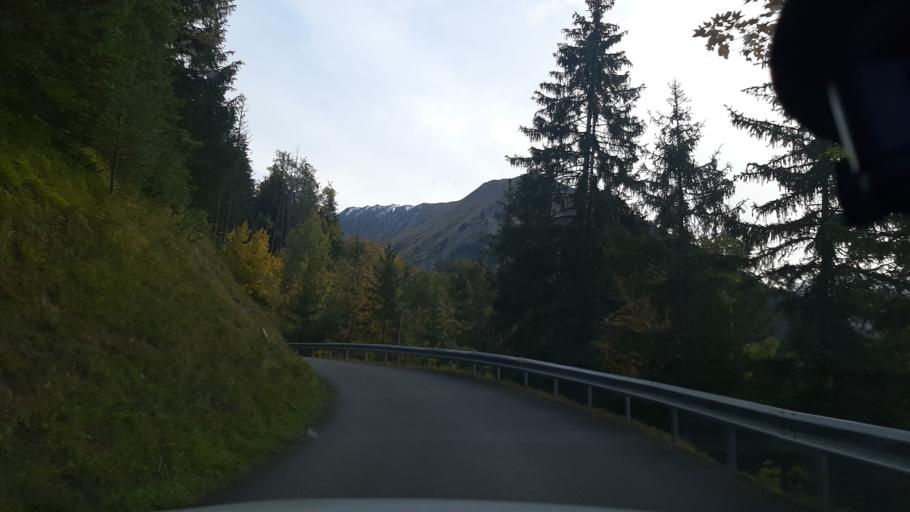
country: FR
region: Rhone-Alpes
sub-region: Departement de la Savoie
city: Saint-Jean-de-Maurienne
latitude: 45.1993
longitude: 6.3103
